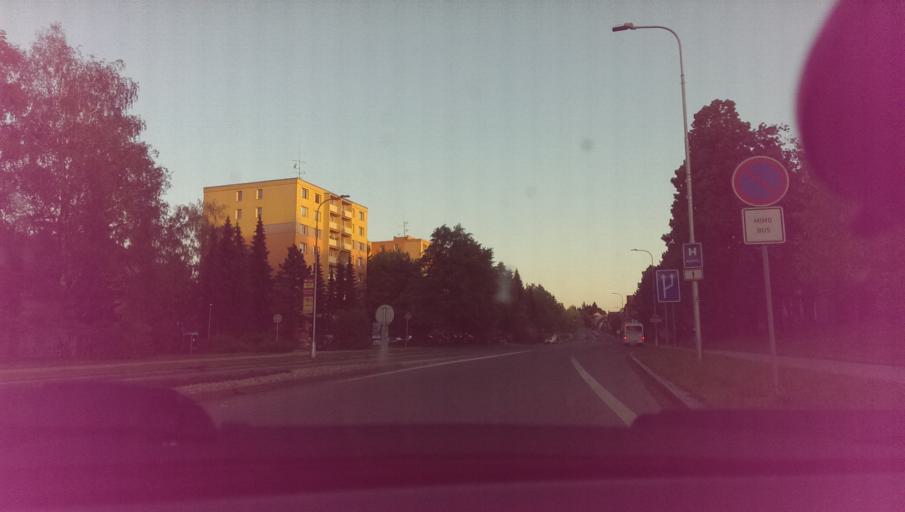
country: CZ
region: Zlin
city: Valasske Mezirici
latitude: 49.4696
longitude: 17.9732
